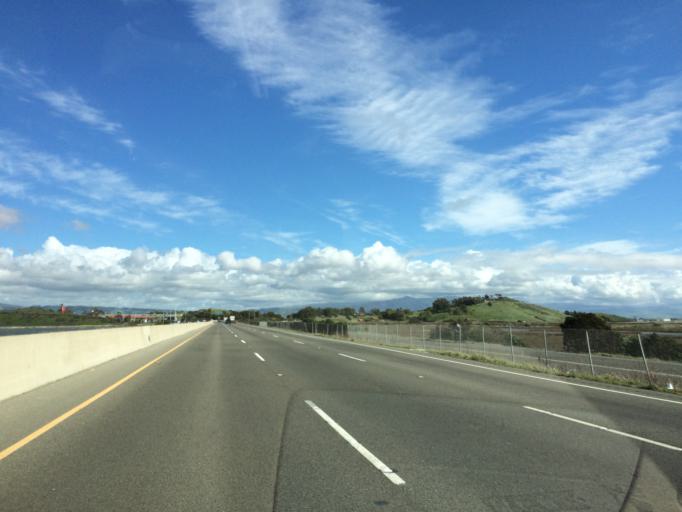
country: US
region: California
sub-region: Alameda County
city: Newark
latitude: 37.5332
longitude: -122.0836
